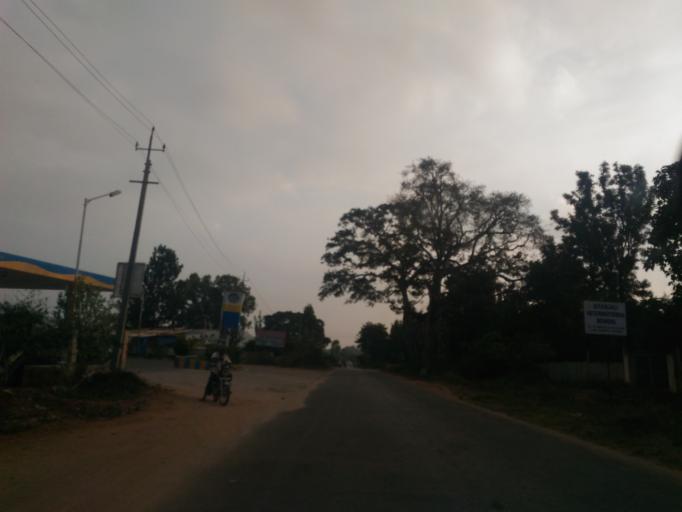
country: IN
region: Karnataka
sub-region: Bangalore Rural
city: Devanhalli
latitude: 13.3264
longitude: 77.6923
